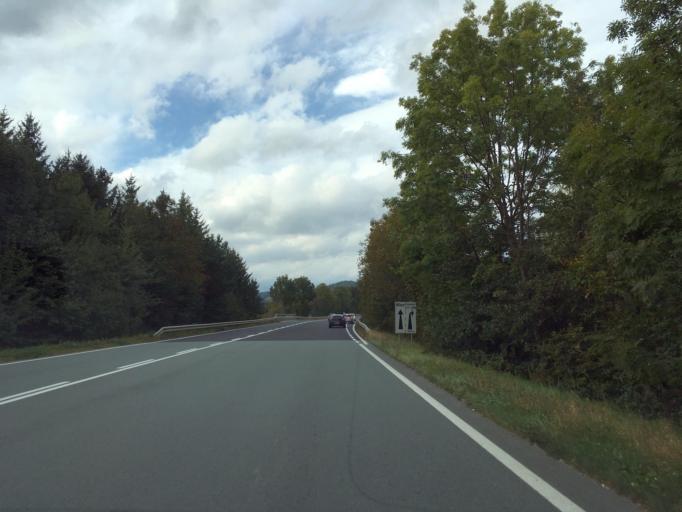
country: AT
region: Styria
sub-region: Politischer Bezirk Hartberg-Fuerstenfeld
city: Rohrbach an der Lafnitz
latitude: 47.3861
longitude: 16.0039
